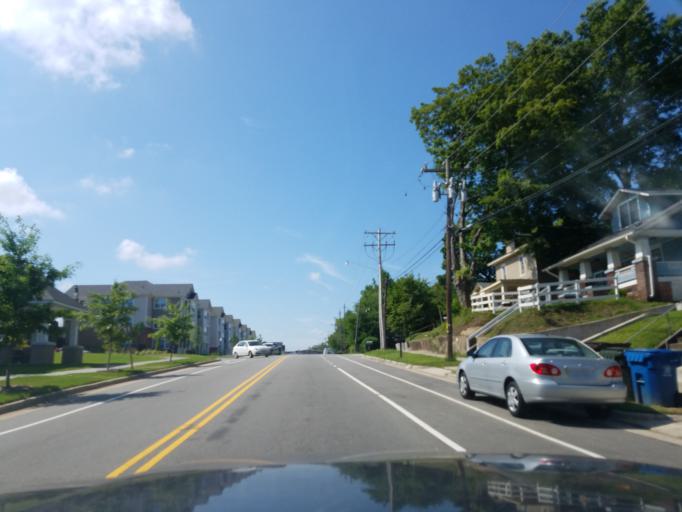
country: US
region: North Carolina
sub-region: Durham County
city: Durham
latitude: 35.9870
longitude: -78.9027
